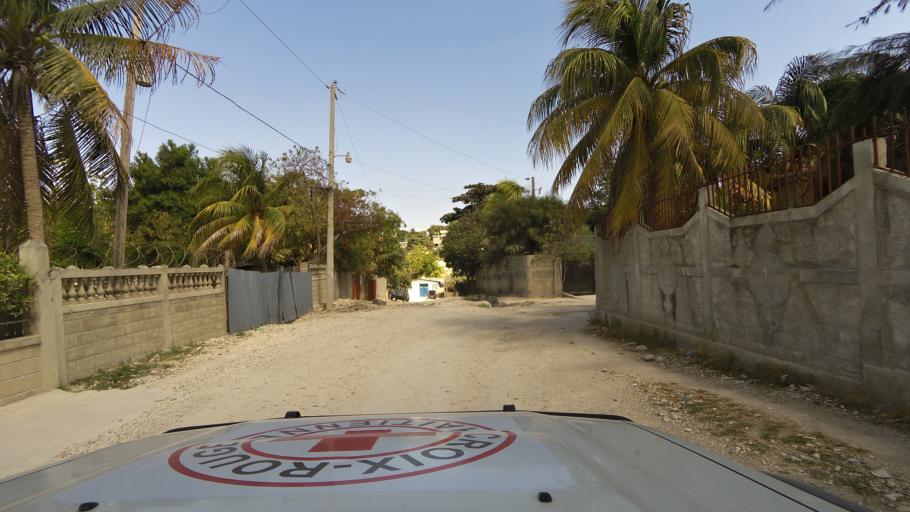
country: HT
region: Ouest
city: Delmas 73
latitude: 18.5604
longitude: -72.2969
